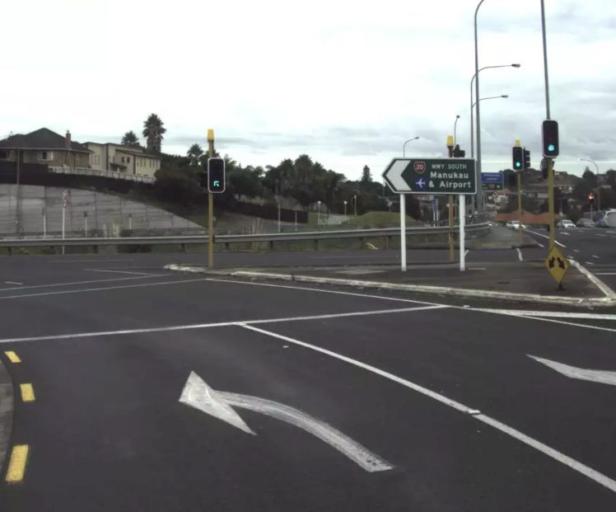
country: NZ
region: Auckland
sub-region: Auckland
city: Auckland
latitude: -36.9172
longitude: 174.7587
